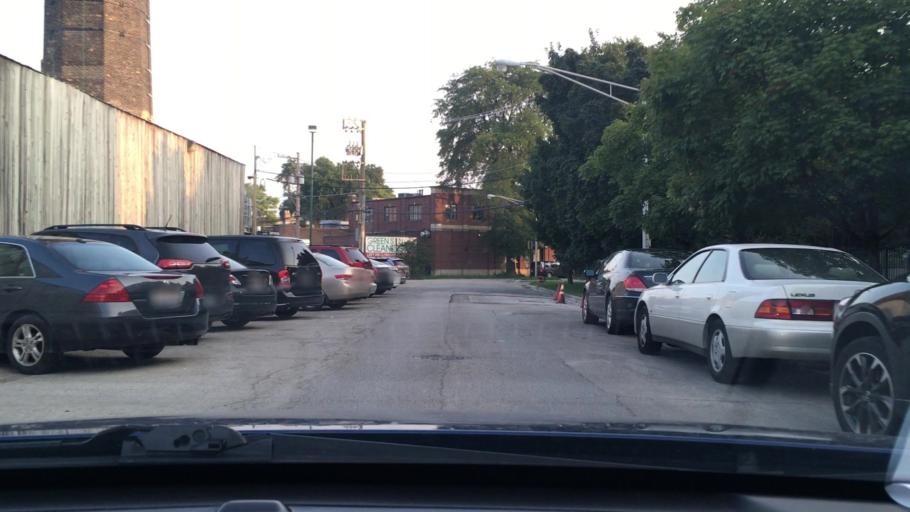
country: US
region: Illinois
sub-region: Cook County
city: Chicago
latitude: 41.9310
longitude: -87.6751
